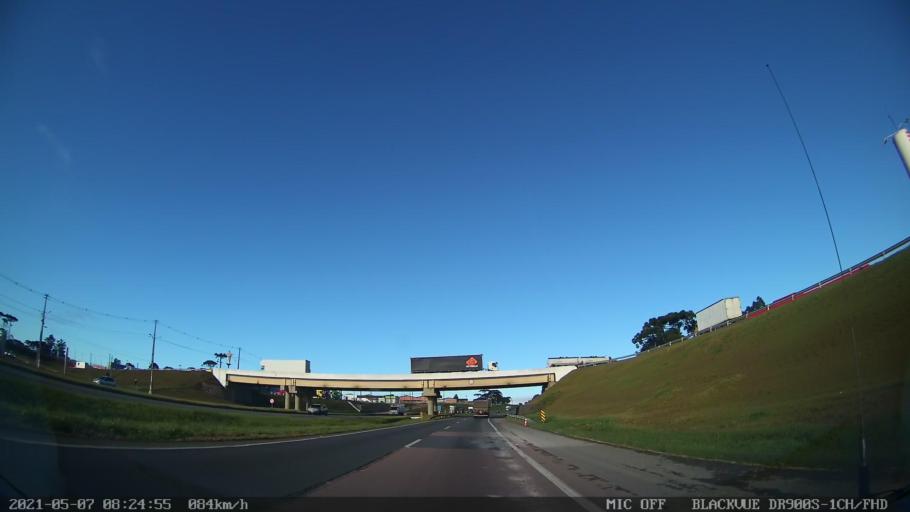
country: BR
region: Parana
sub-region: Sao Jose Dos Pinhais
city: Sao Jose dos Pinhais
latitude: -25.5681
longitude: -49.1779
